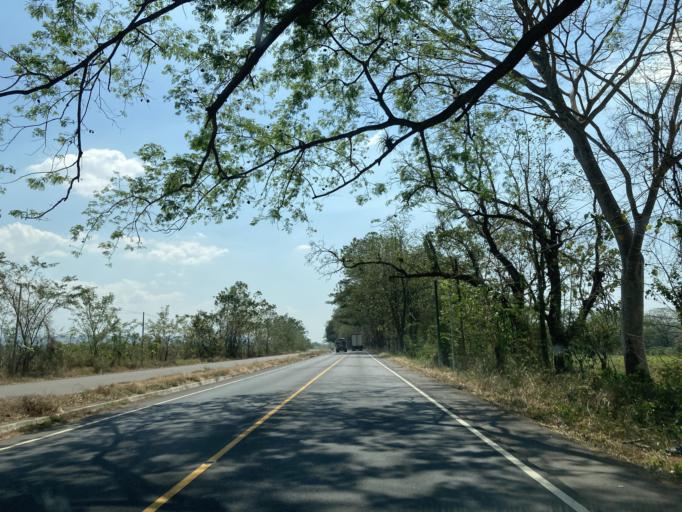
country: GT
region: Escuintla
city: Guanagazapa
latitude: 14.2014
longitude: -90.7030
